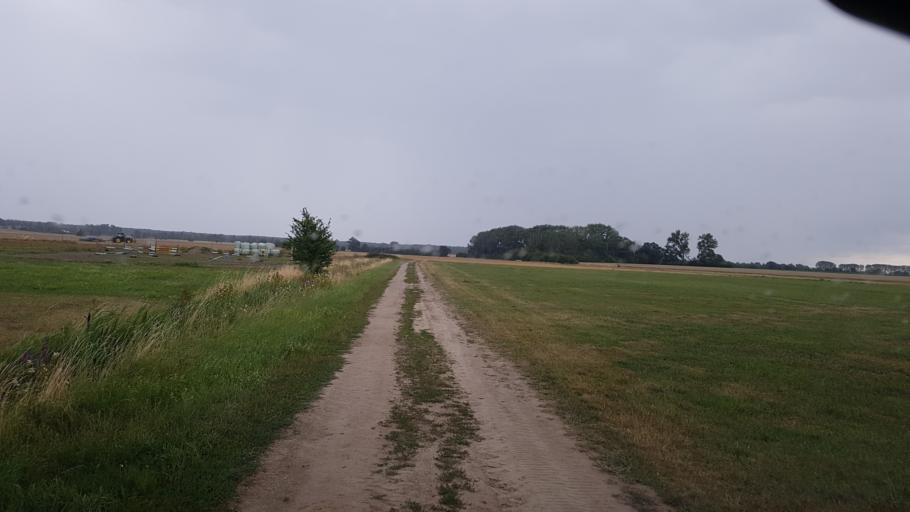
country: DE
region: Brandenburg
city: Sonnewalde
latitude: 51.7040
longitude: 13.6983
